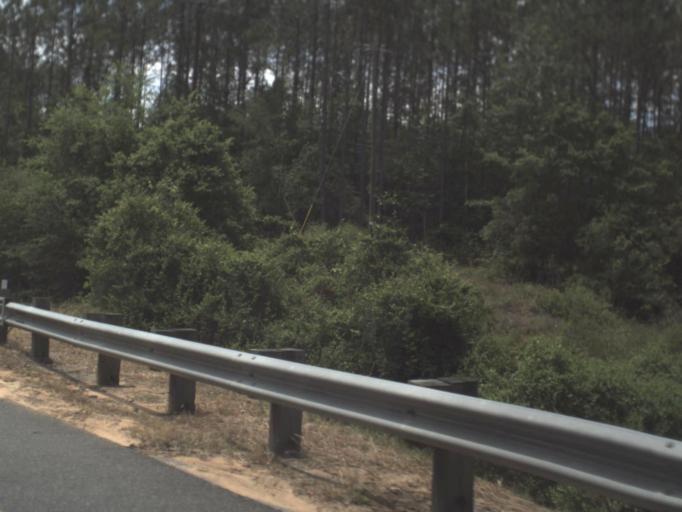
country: US
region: Florida
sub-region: Gulf County
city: Wewahitchka
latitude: 30.2567
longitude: -85.1989
